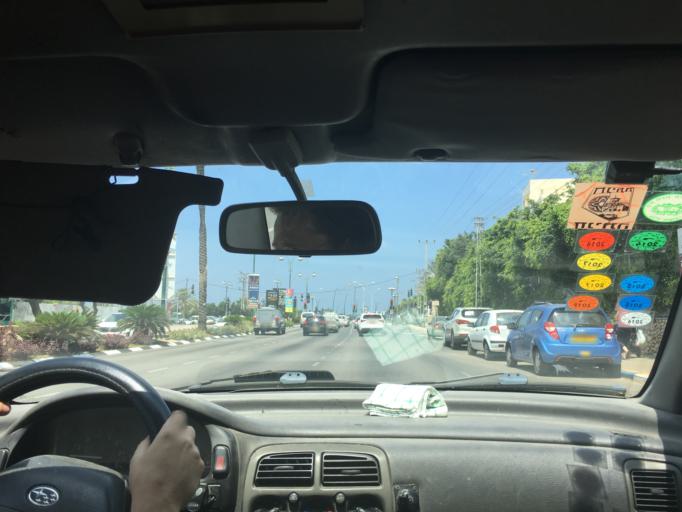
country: IL
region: Tel Aviv
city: Ramat HaSharon
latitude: 32.1381
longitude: 34.8364
